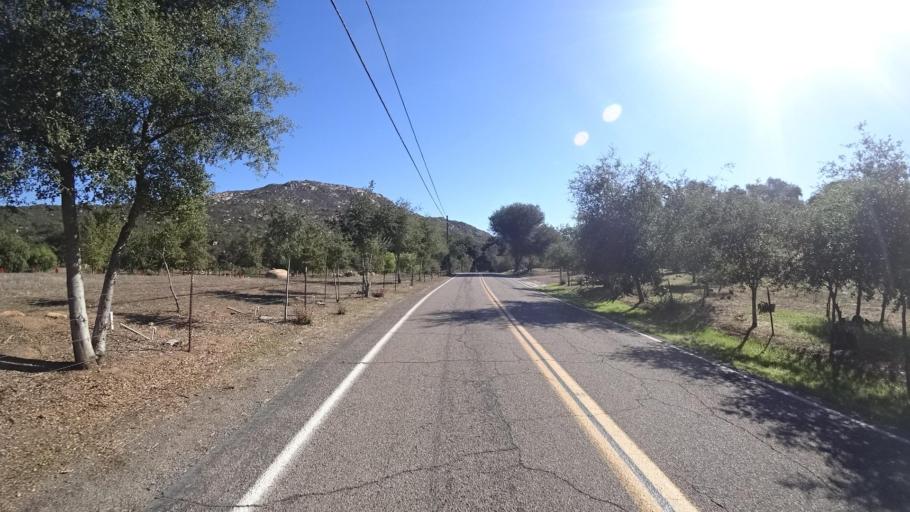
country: US
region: California
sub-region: San Diego County
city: Jamul
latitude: 32.7141
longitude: -116.7584
